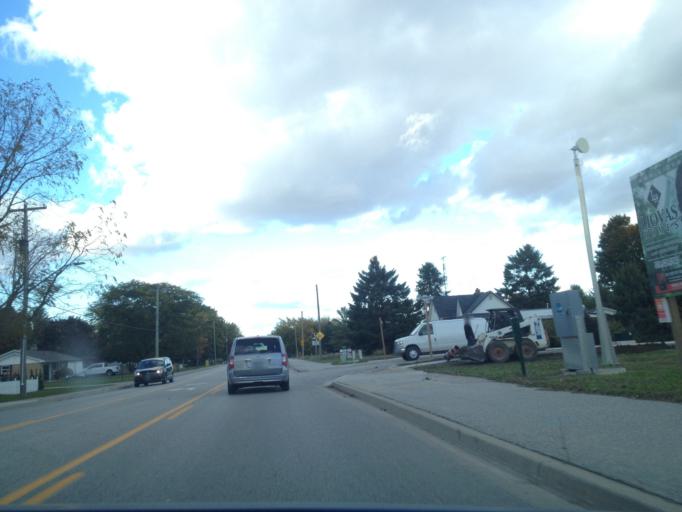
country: CA
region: Ontario
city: Amherstburg
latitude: 42.0463
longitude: -82.7389
